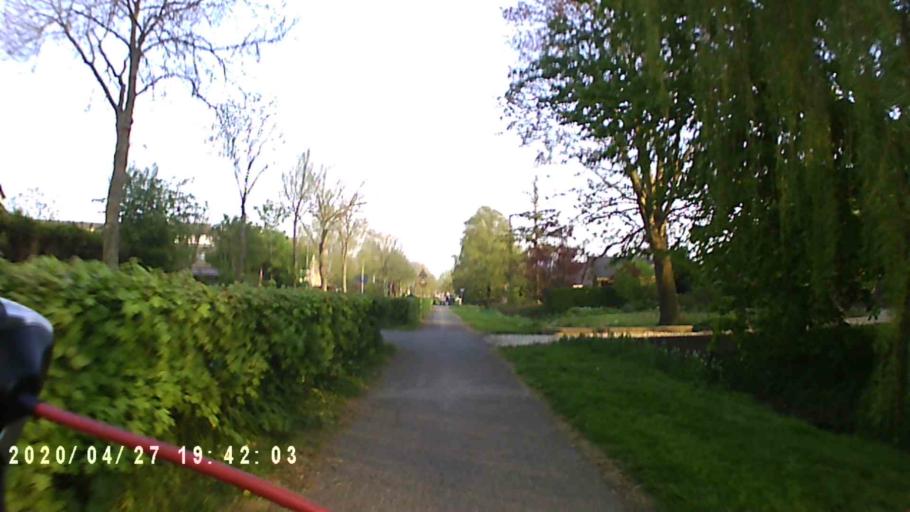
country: NL
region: Groningen
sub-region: Gemeente Winsum
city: Winsum
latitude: 53.3602
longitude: 6.4623
